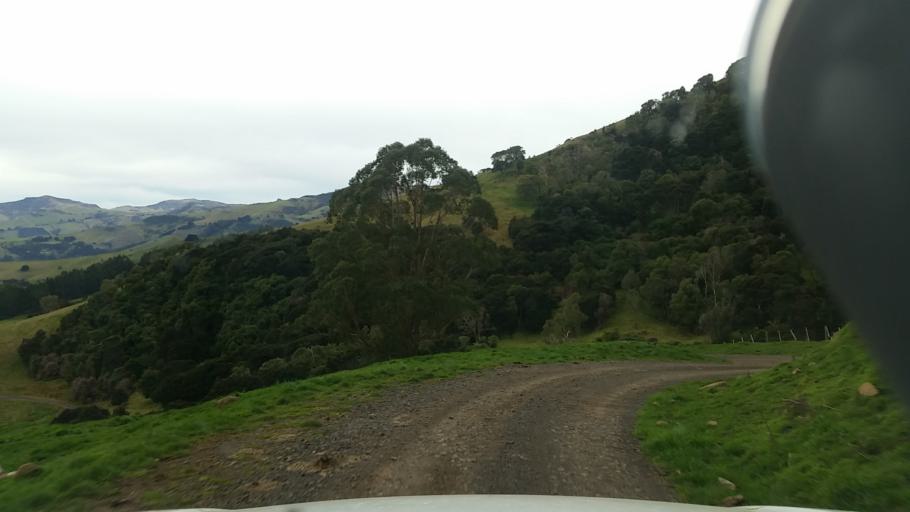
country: NZ
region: Canterbury
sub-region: Christchurch City
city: Christchurch
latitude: -43.8189
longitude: 172.9913
